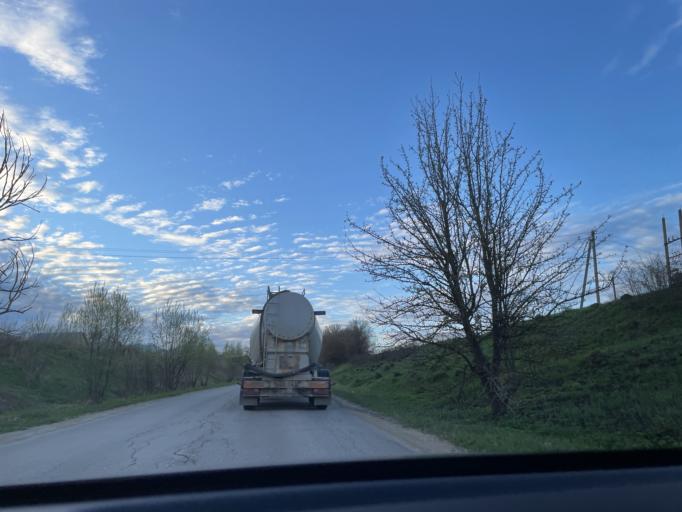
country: RU
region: Moskovskaya
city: Serpukhov
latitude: 54.8273
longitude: 37.4283
